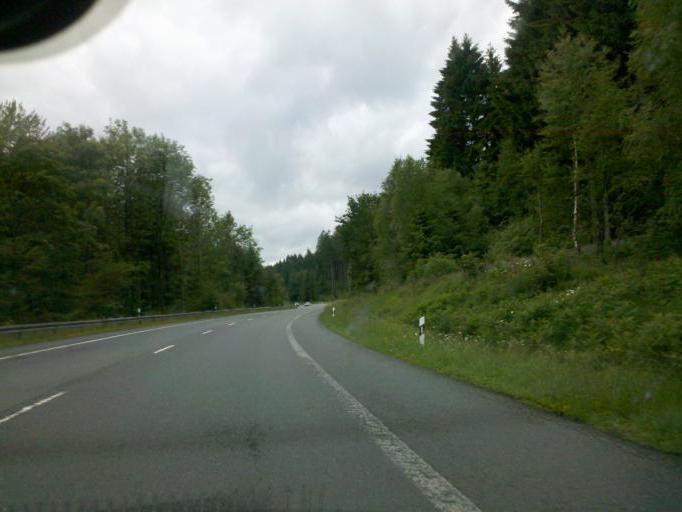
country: DE
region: North Rhine-Westphalia
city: Warstein
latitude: 51.4096
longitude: 8.3239
